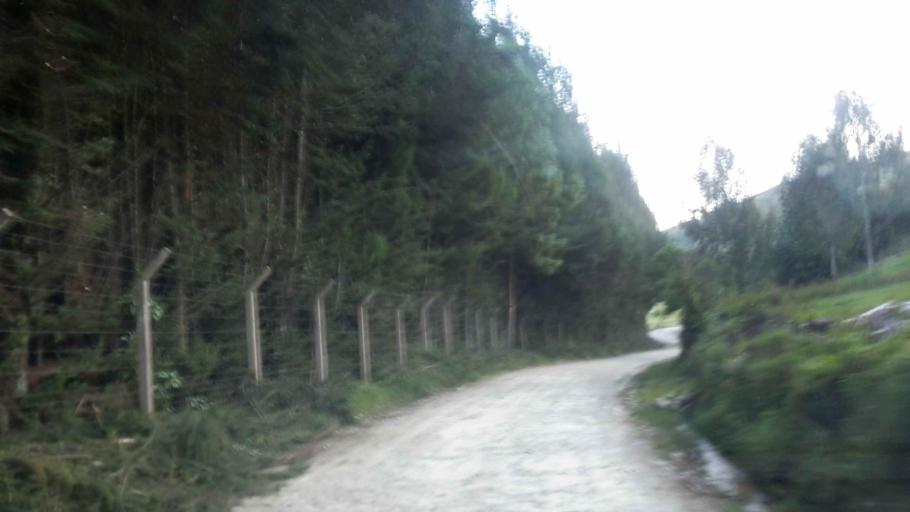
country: BO
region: Cochabamba
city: Colomi
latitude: -17.2427
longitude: -65.9046
